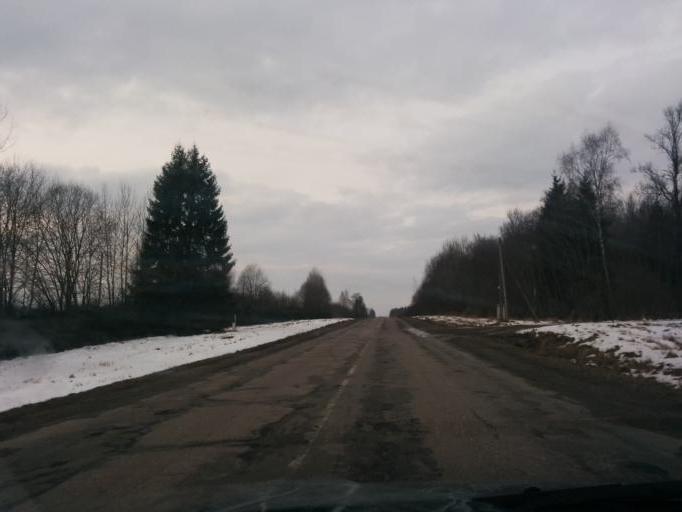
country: LV
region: Balvu Rajons
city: Balvi
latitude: 57.1516
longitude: 27.2235
